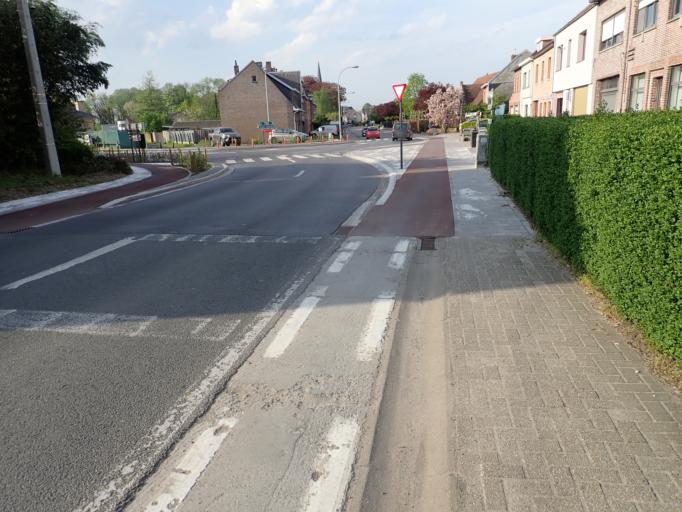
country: BE
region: Flanders
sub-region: Provincie Vlaams-Brabant
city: Londerzeel
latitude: 50.9967
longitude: 4.3022
